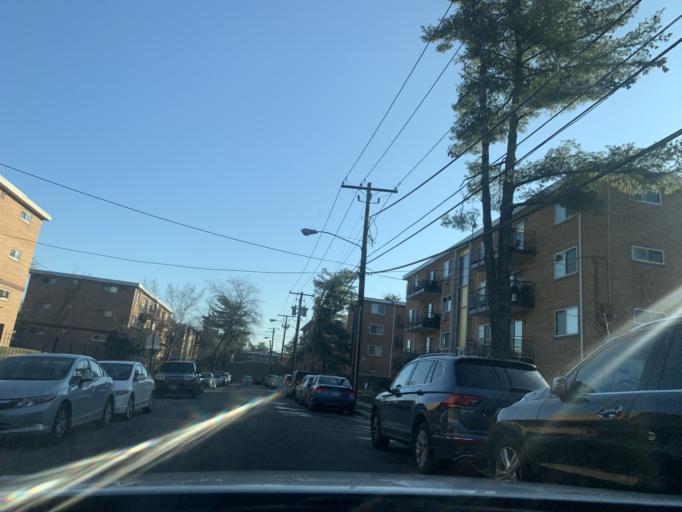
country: US
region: Maryland
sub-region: Prince George's County
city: Capitol Heights
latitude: 38.8909
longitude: -76.9439
